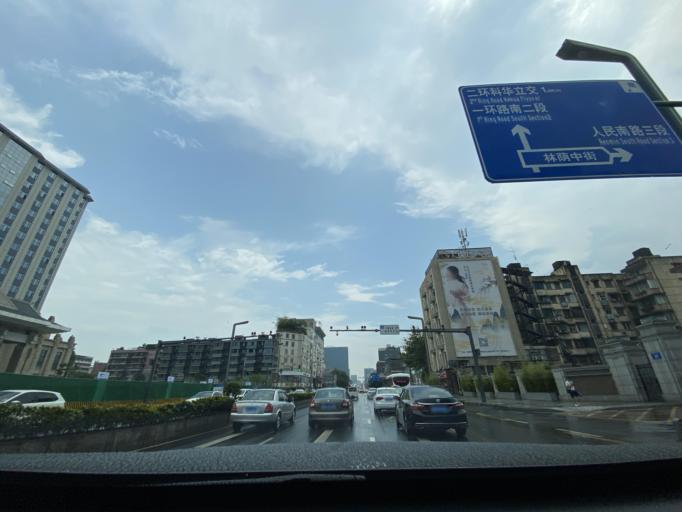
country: CN
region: Sichuan
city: Chengdu
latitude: 30.6397
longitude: 104.0734
